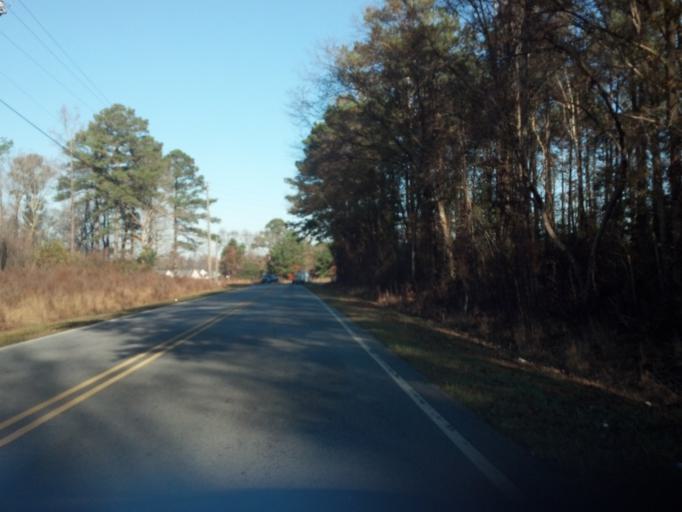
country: US
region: North Carolina
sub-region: Pitt County
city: Winterville
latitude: 35.5416
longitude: -77.4424
